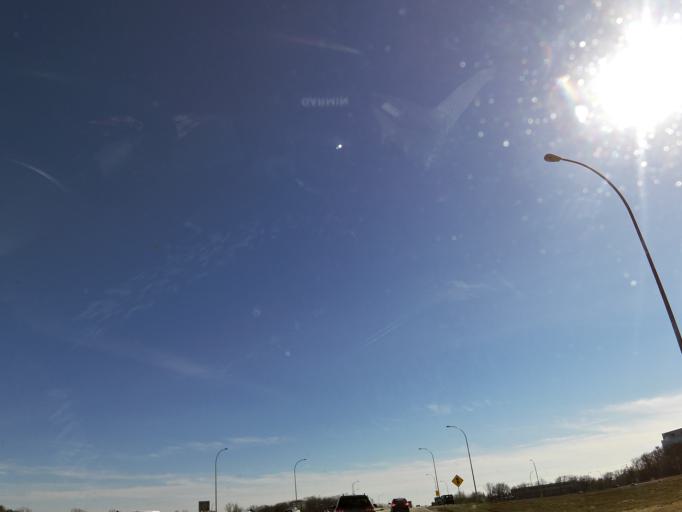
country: US
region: Minnesota
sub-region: Hennepin County
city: Edina
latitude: 44.8925
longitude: -93.3997
